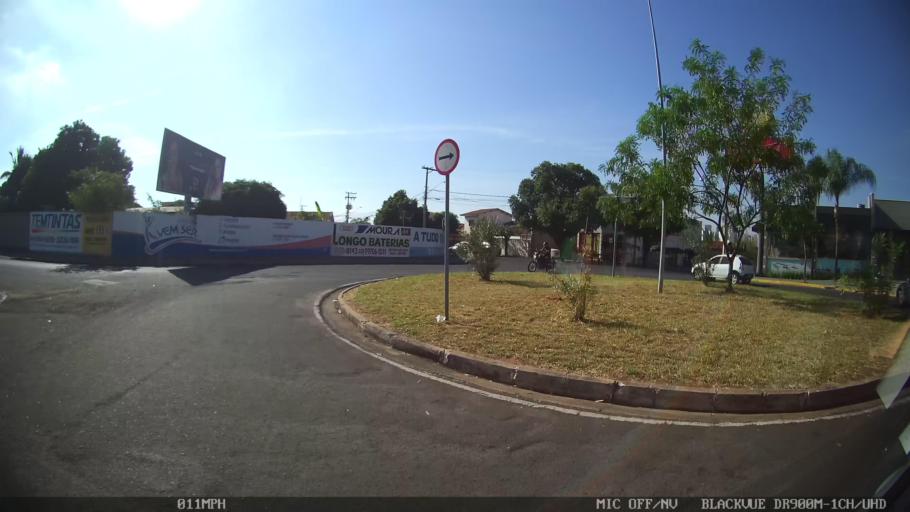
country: BR
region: Sao Paulo
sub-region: Sao Jose Do Rio Preto
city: Sao Jose do Rio Preto
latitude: -20.8120
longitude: -49.3983
